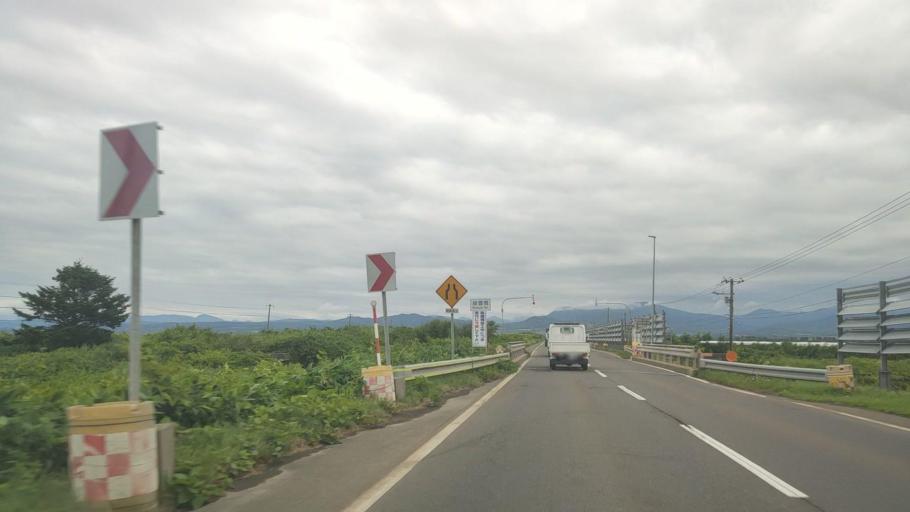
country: JP
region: Hokkaido
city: Nanae
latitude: 42.3039
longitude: 140.2721
